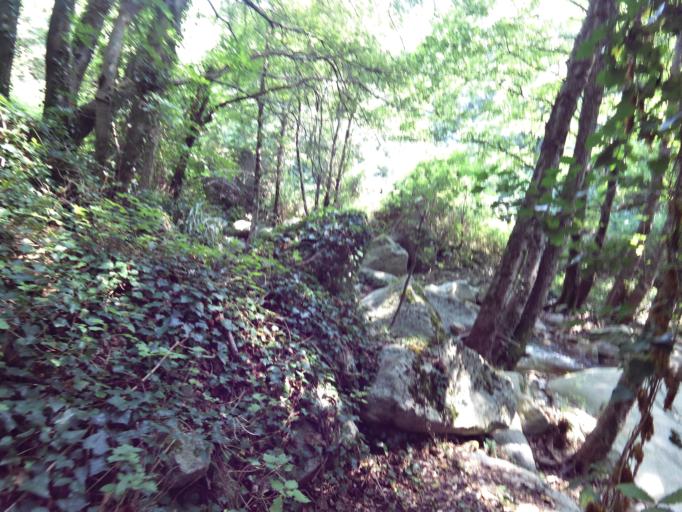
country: IT
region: Calabria
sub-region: Provincia di Reggio Calabria
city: Bivongi
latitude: 38.5000
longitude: 16.3984
